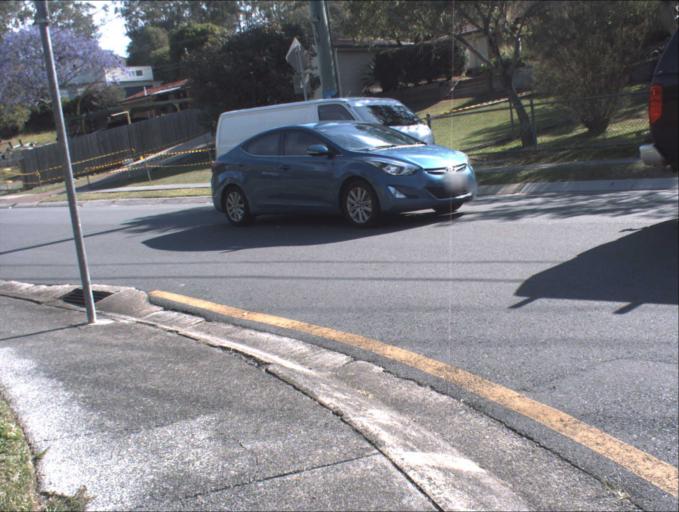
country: AU
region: Queensland
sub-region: Logan
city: Slacks Creek
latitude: -27.6487
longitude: 153.1780
